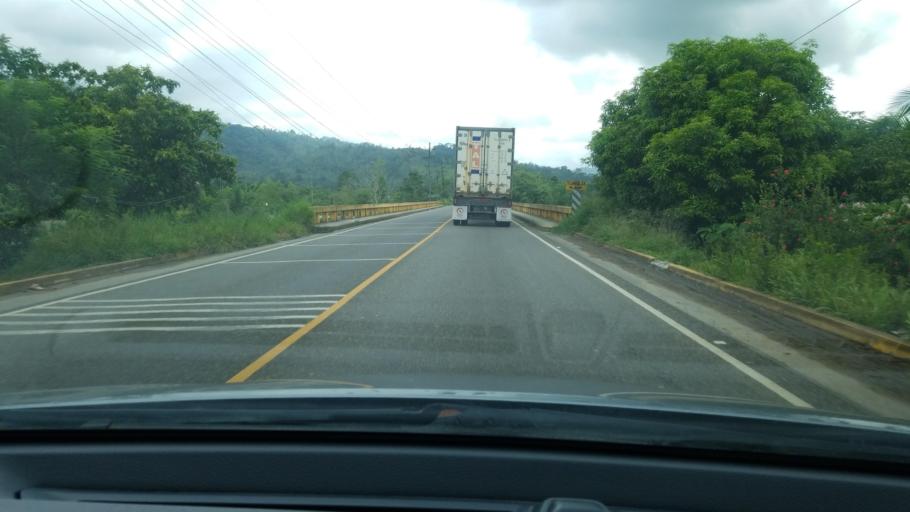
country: HN
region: Cortes
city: Potrerillos
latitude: 15.5910
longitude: -88.3260
